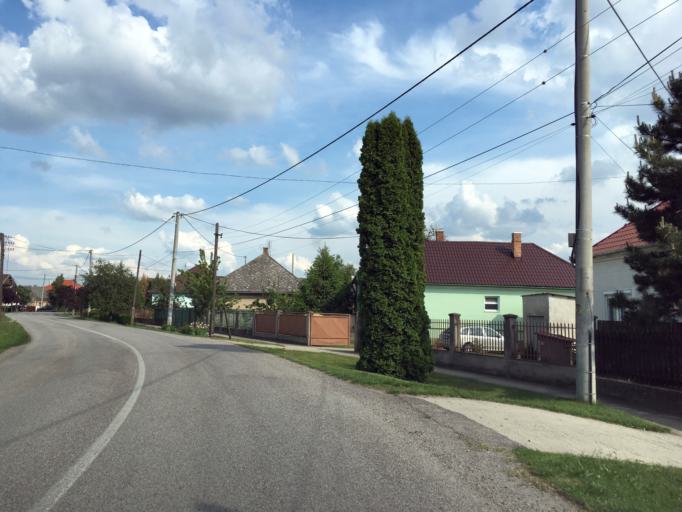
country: SK
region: Nitriansky
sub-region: Okres Komarno
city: Hurbanovo
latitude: 47.8114
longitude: 18.2221
